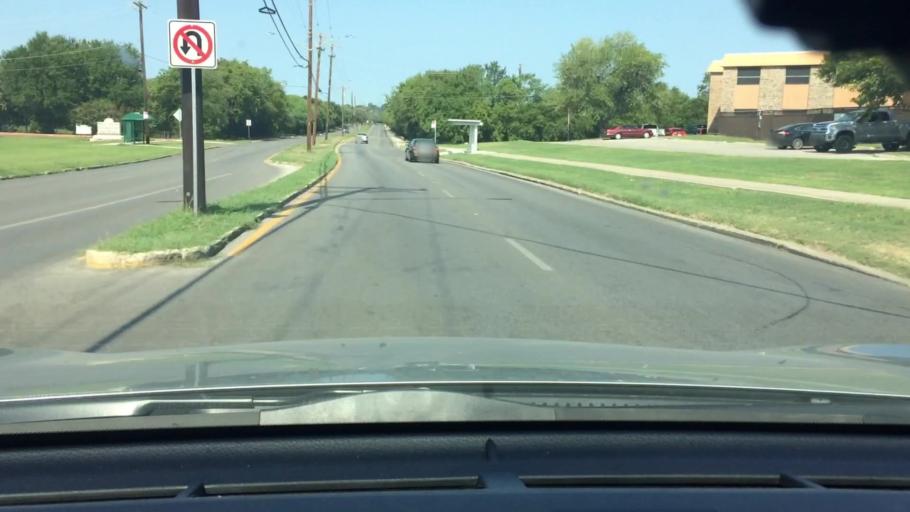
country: US
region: Texas
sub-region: Bexar County
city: China Grove
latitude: 29.3748
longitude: -98.4200
